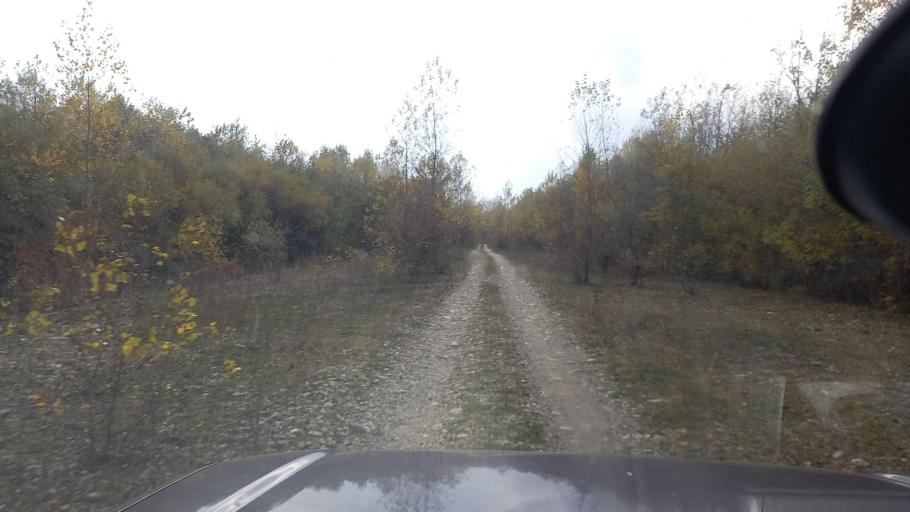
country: RU
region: Krasnodarskiy
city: Shedok
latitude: 44.1725
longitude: 40.8483
